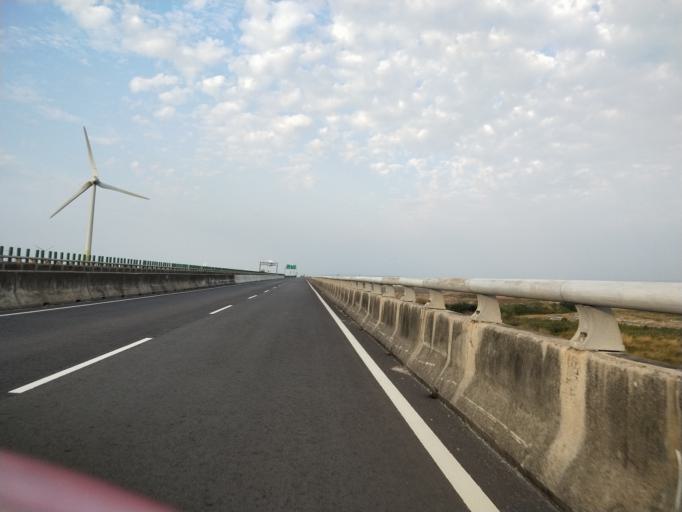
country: TW
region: Taiwan
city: Fengyuan
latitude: 24.4005
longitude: 120.6100
